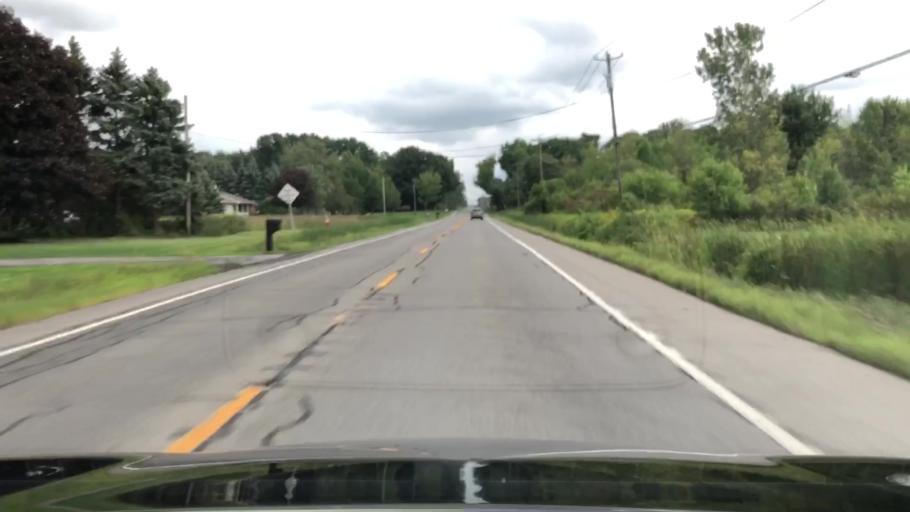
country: US
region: New York
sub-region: Erie County
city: Orchard Park
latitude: 42.7993
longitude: -78.6969
